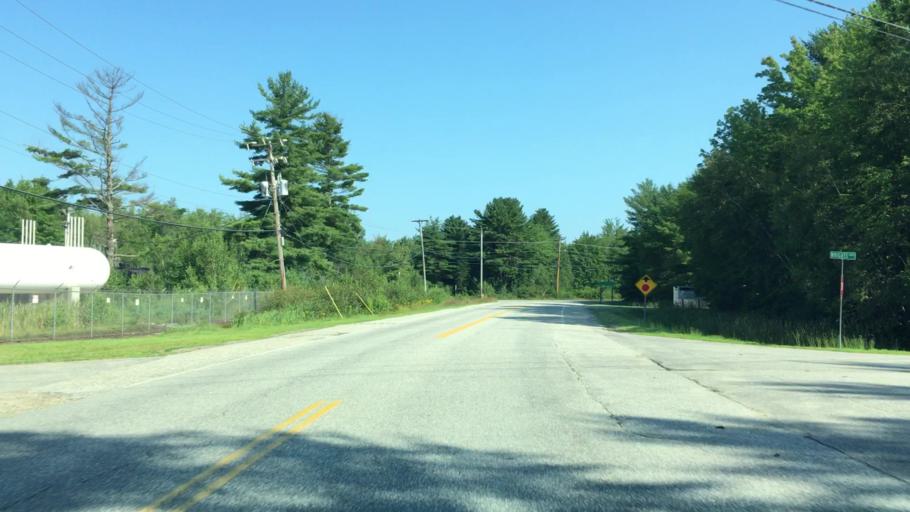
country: US
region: Maine
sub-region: Androscoggin County
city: Minot
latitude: 44.0461
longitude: -70.2954
